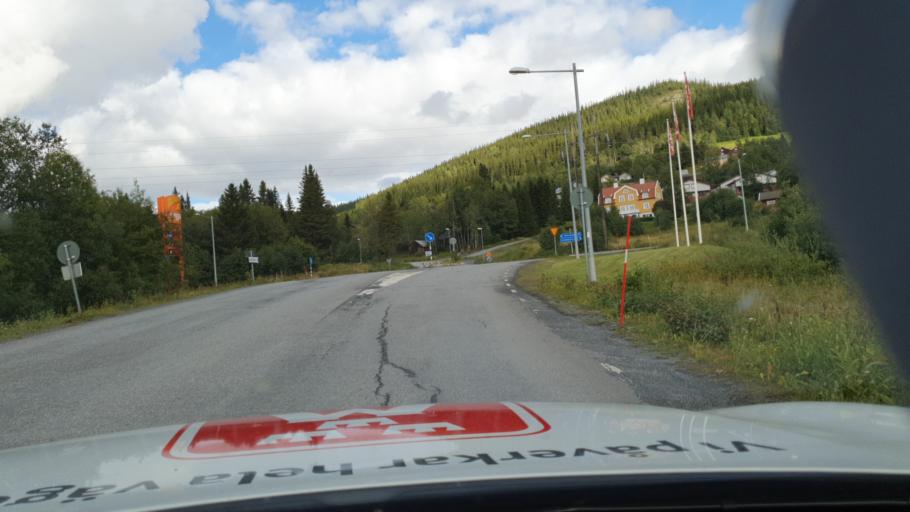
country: SE
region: Jaemtland
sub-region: Are Kommun
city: Are
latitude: 63.3950
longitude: 12.9162
